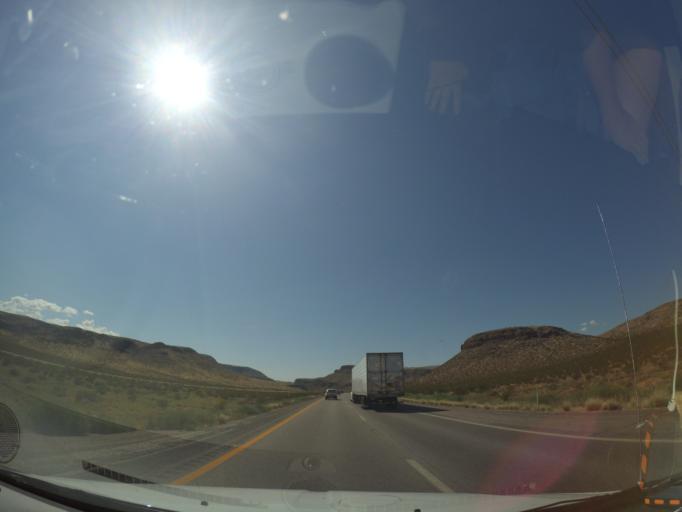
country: US
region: Utah
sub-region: Washington County
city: Saint George
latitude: 36.9811
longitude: -113.6562
